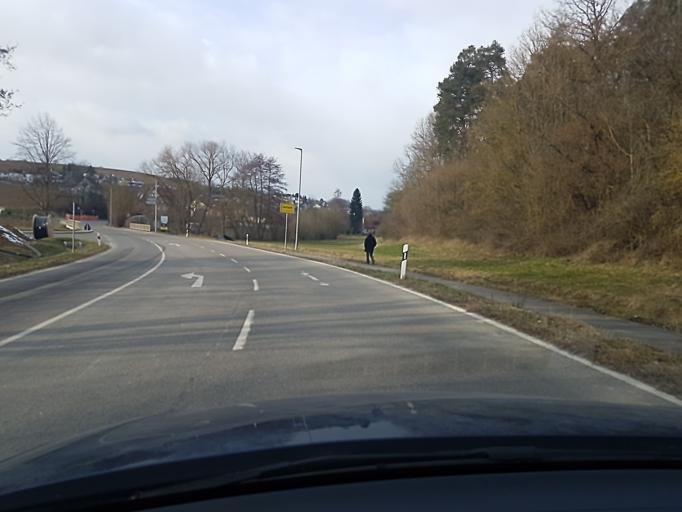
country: DE
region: Baden-Wuerttemberg
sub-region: Regierungsbezirk Stuttgart
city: Eberdingen
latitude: 48.8722
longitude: 8.9662
